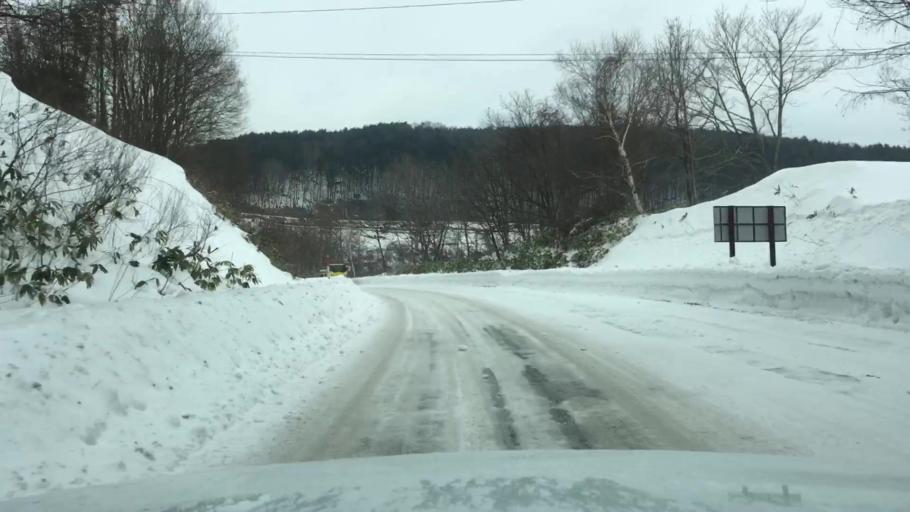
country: JP
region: Iwate
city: Shizukuishi
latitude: 39.9484
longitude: 140.9985
